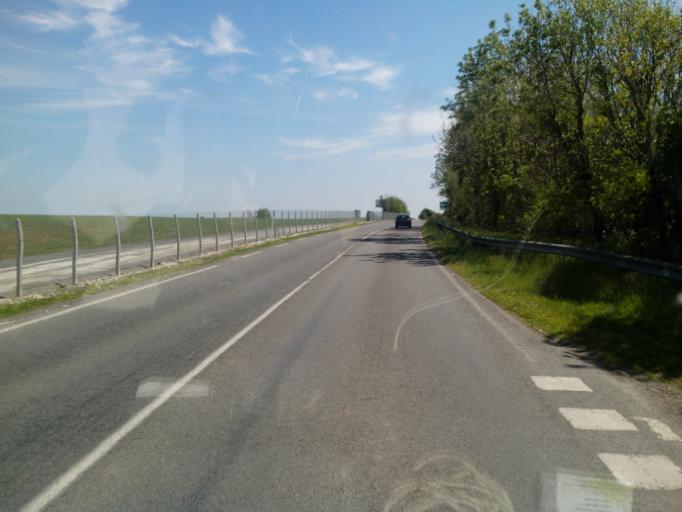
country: FR
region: Nord-Pas-de-Calais
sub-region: Departement du Pas-de-Calais
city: Samer
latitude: 50.5707
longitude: 1.7503
